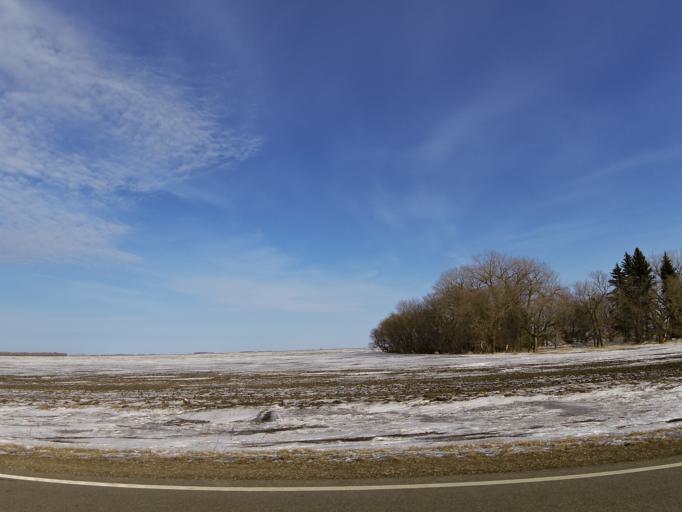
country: US
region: Minnesota
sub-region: Kittson County
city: Hallock
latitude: 48.5599
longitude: -97.1067
